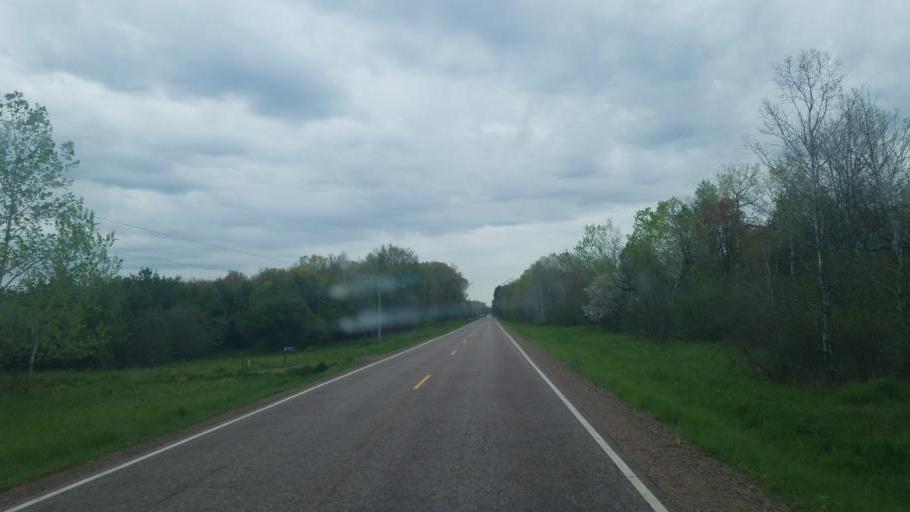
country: US
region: Wisconsin
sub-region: Wood County
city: Marshfield
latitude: 44.4566
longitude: -90.2799
